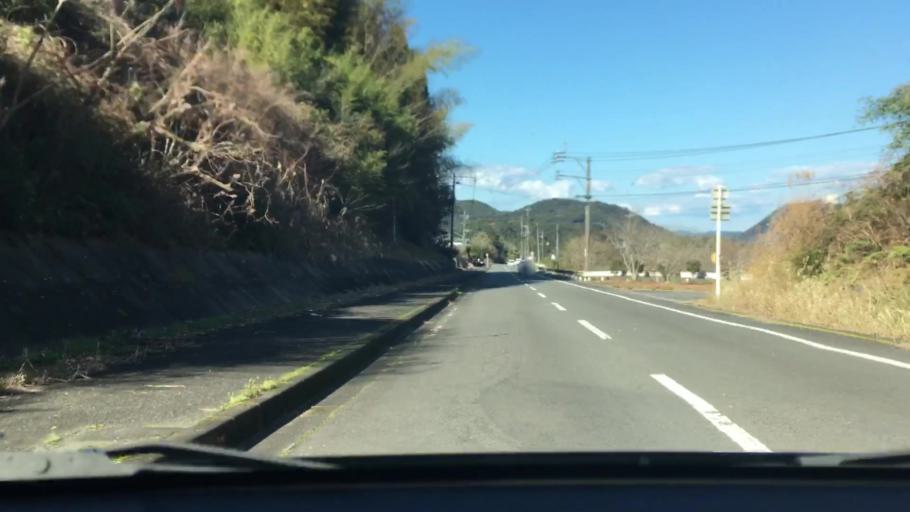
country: JP
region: Kagoshima
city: Satsumasendai
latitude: 31.7698
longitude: 130.4017
